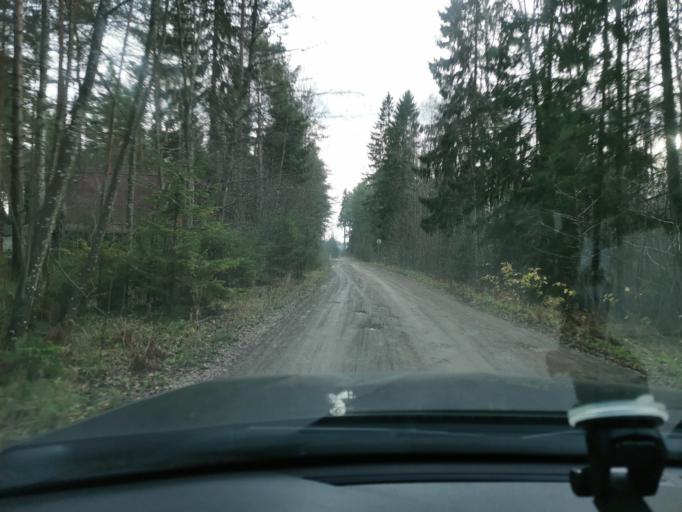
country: EE
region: Ida-Virumaa
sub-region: Sillamaee linn
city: Sillamae
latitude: 59.2553
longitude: 27.9134
